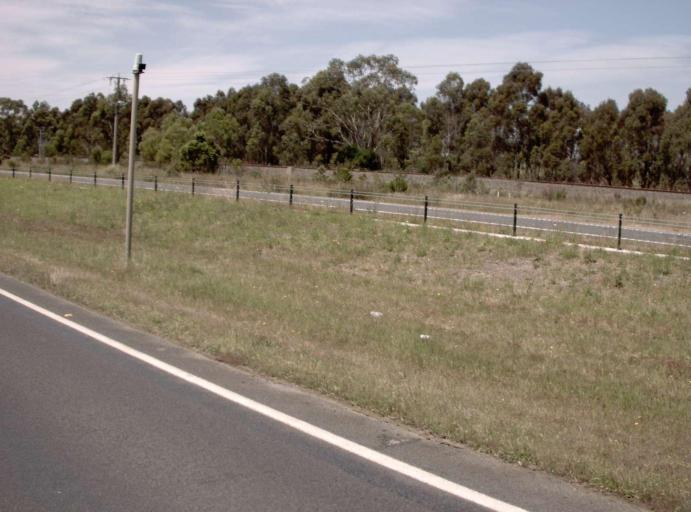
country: AU
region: Victoria
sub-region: Latrobe
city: Morwell
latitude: -38.2236
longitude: 146.4673
